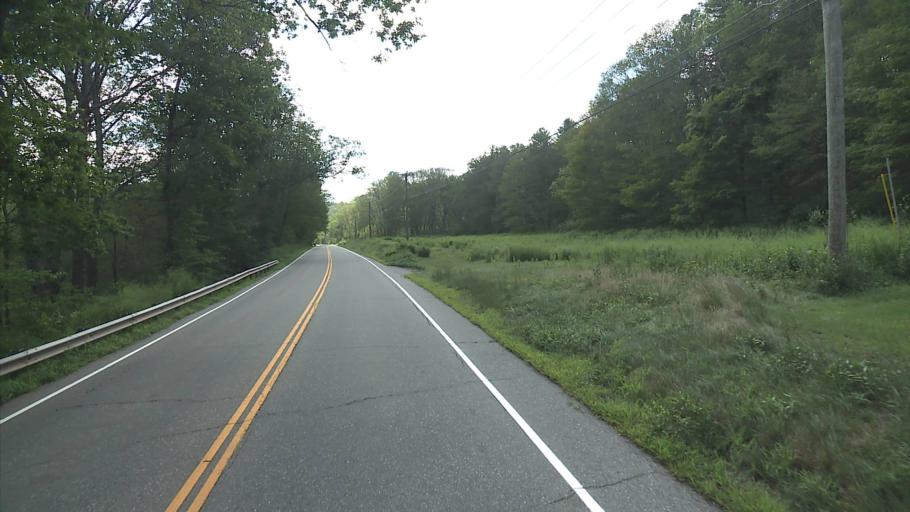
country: US
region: Connecticut
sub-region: Windham County
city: South Woodstock
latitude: 41.8635
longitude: -72.0934
